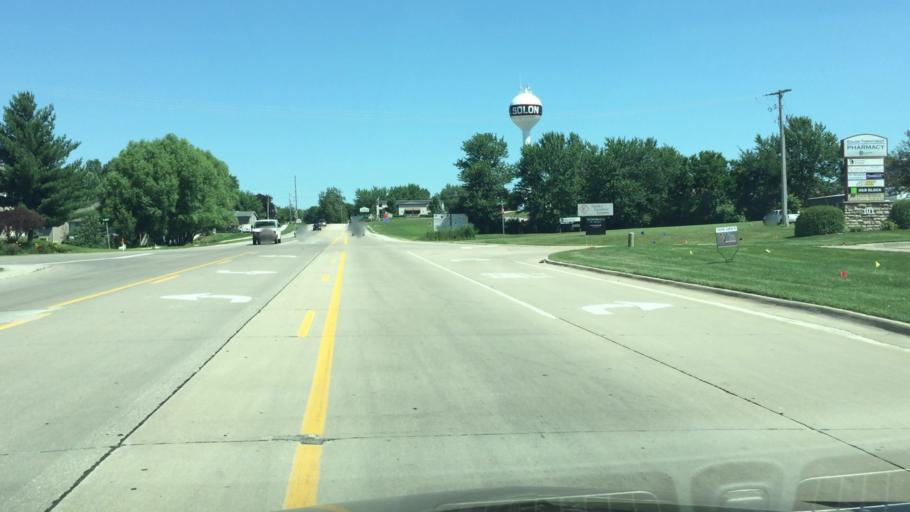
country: US
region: Iowa
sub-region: Johnson County
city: Solon
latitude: 41.7987
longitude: -91.4909
